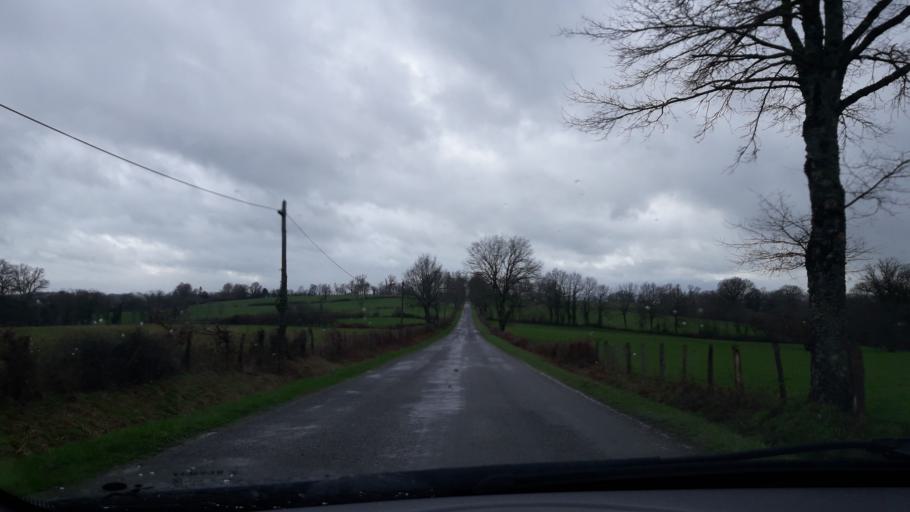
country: FR
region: Limousin
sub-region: Departement de la Haute-Vienne
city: Saint-Paul
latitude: 45.7535
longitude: 1.4167
